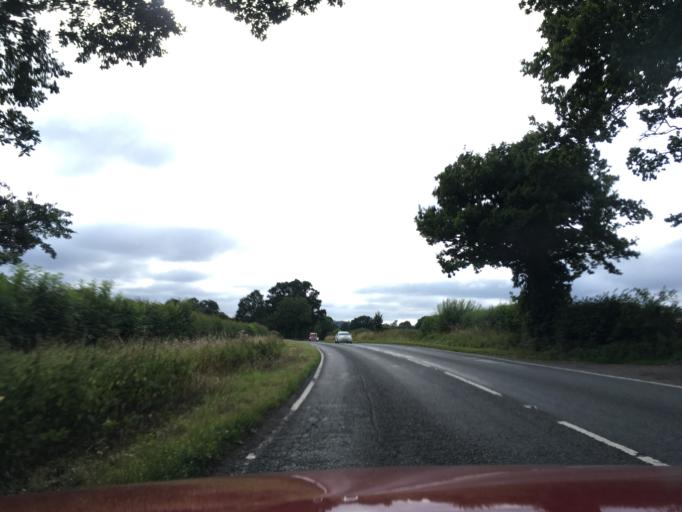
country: GB
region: England
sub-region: Hampshire
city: Four Marks
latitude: 51.0309
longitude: -1.0648
